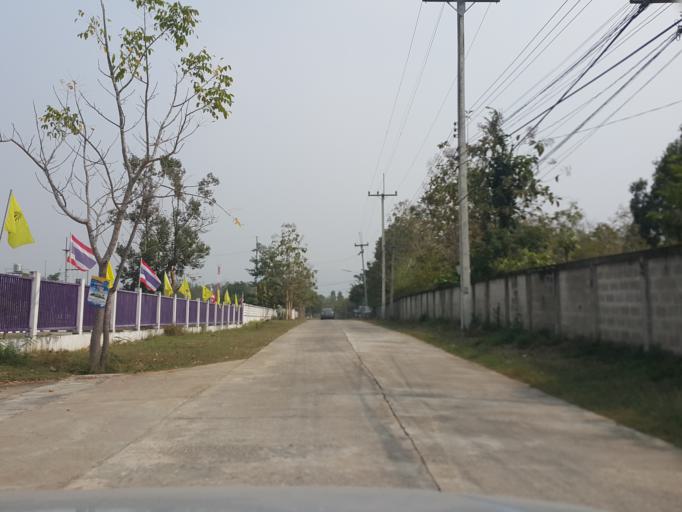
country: TH
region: Lampang
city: Thoen
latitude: 17.6364
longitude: 99.2435
